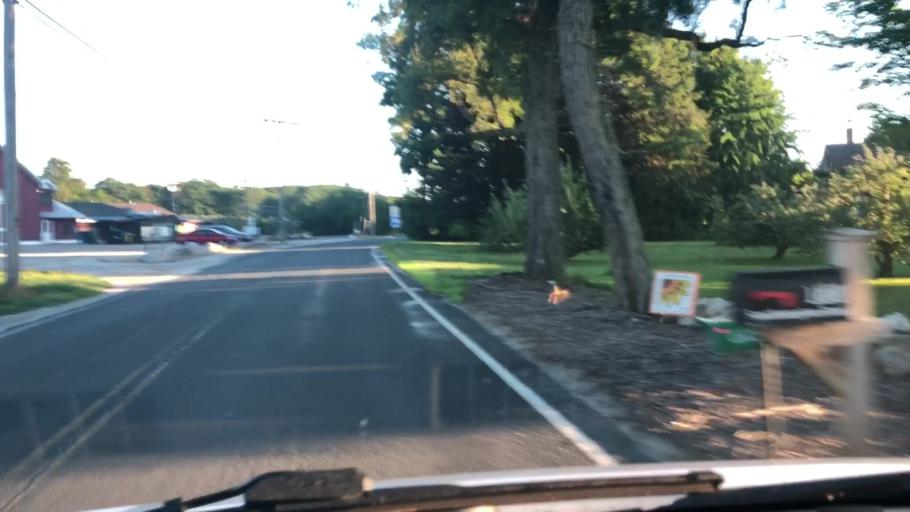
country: US
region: Massachusetts
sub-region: Hampshire County
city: Westhampton
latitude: 42.2865
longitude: -72.7601
